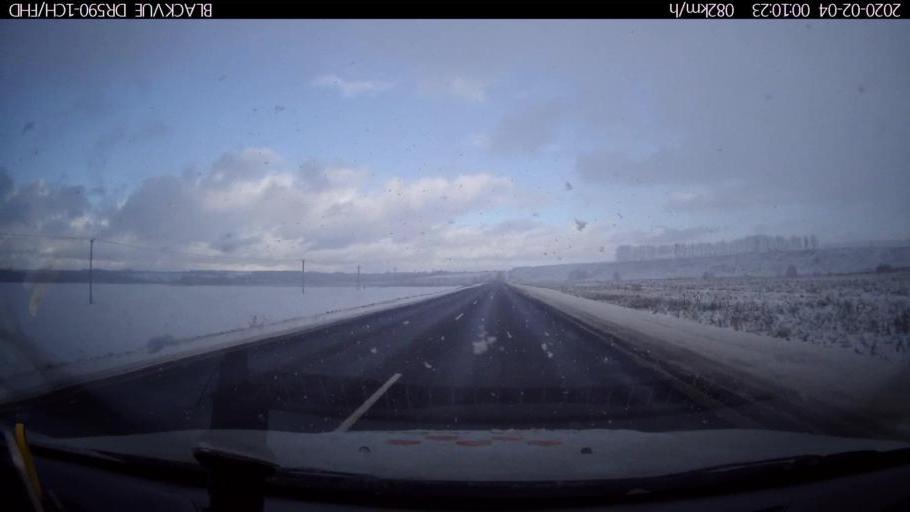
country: RU
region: Nizjnij Novgorod
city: Dal'neye Konstantinovo
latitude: 55.8918
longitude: 44.1479
